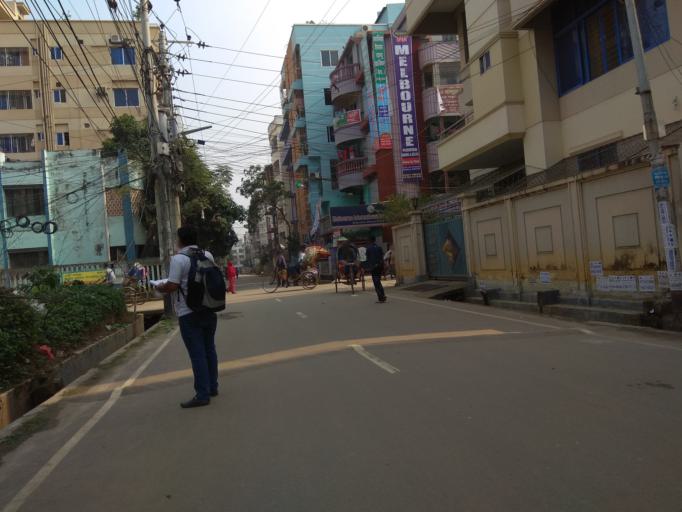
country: BD
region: Dhaka
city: Tungi
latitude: 23.8635
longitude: 90.3876
